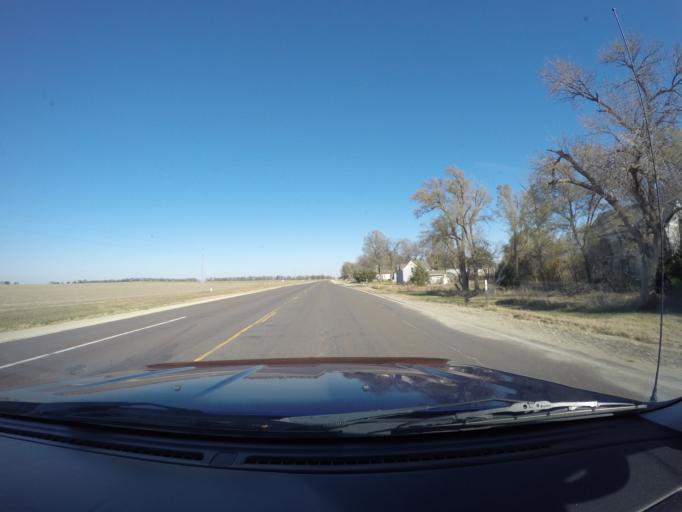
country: US
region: Kansas
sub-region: Marshall County
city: Blue Rapids
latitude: 39.5962
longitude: -96.7500
